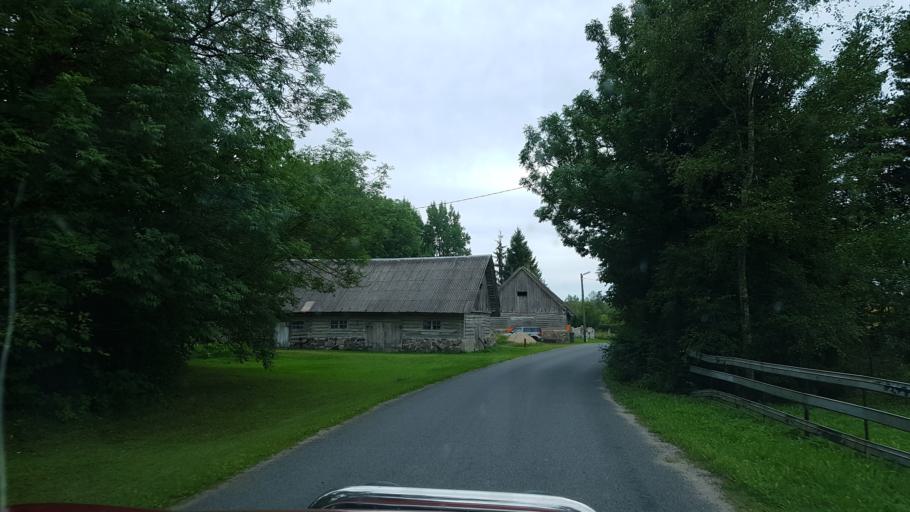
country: EE
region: Laeaene
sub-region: Ridala Parish
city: Uuemoisa
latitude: 58.8028
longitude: 23.6655
